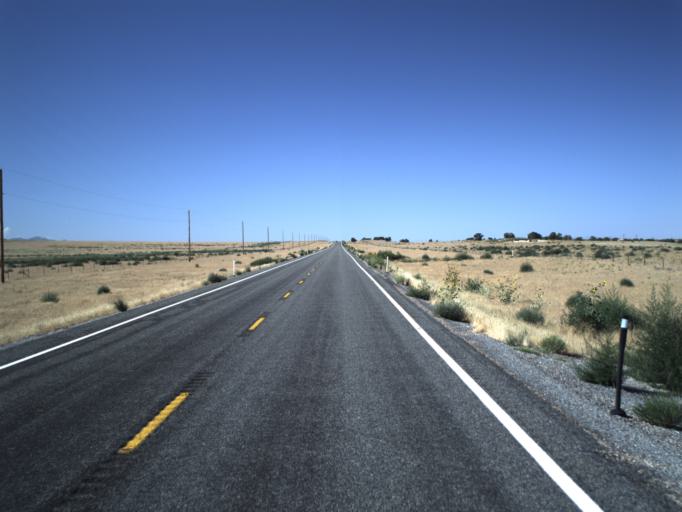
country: US
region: Utah
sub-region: Millard County
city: Delta
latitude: 39.6395
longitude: -112.3050
